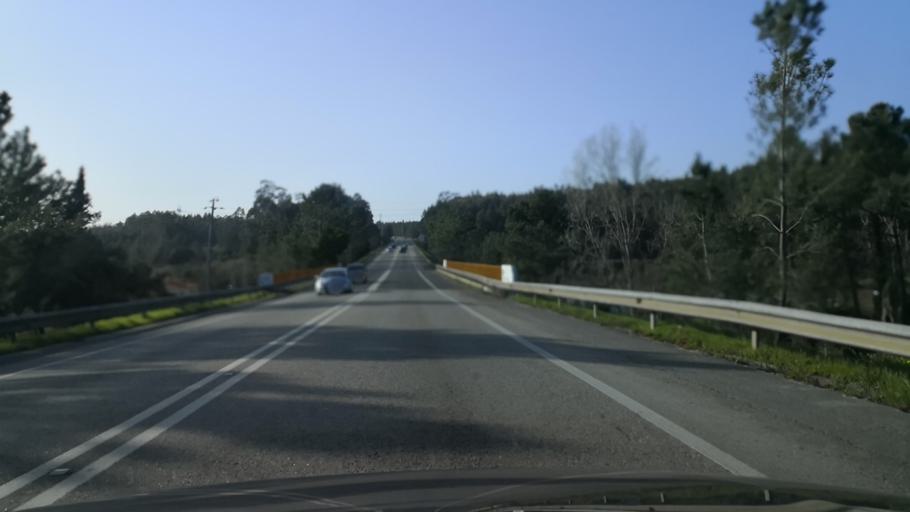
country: PT
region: Leiria
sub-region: Leiria
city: Leiria
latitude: 39.7447
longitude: -8.8482
